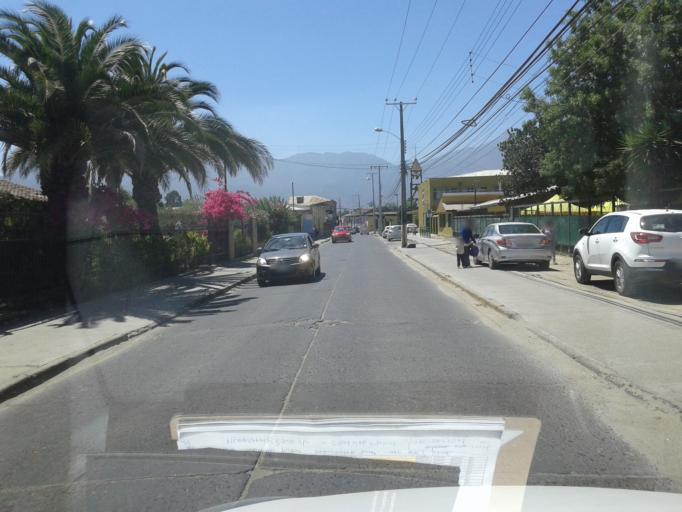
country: CL
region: Valparaiso
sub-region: Provincia de Quillota
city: Quillota
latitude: -32.8720
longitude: -71.2448
